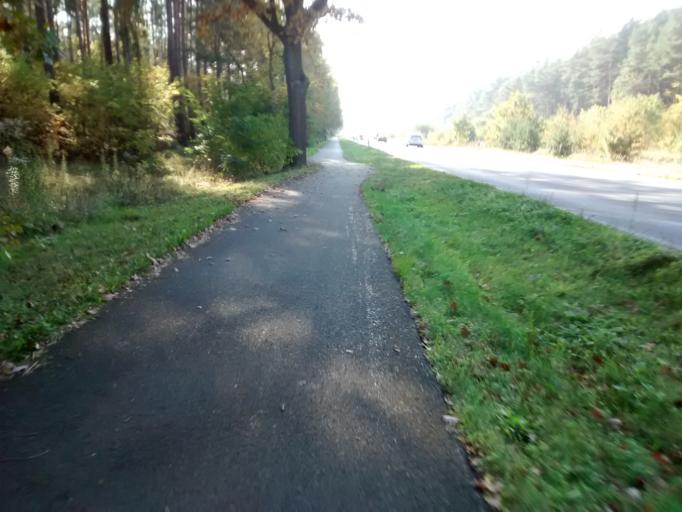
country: DE
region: Berlin
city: Heiligensee
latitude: 52.6491
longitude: 13.2379
